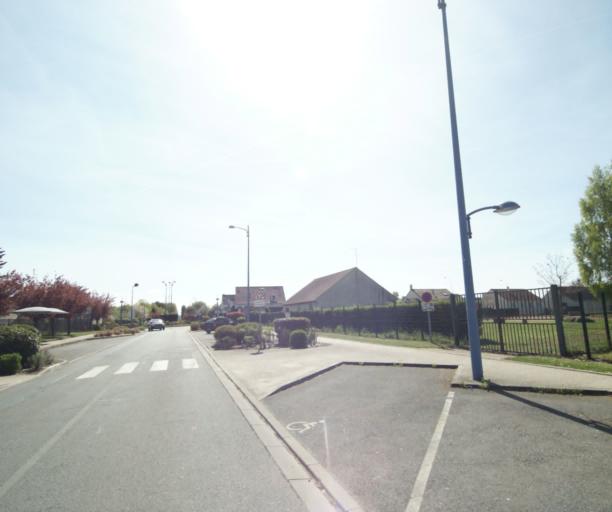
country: FR
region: Ile-de-France
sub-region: Departement de Seine-et-Marne
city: Nangis
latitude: 48.5513
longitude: 3.0157
